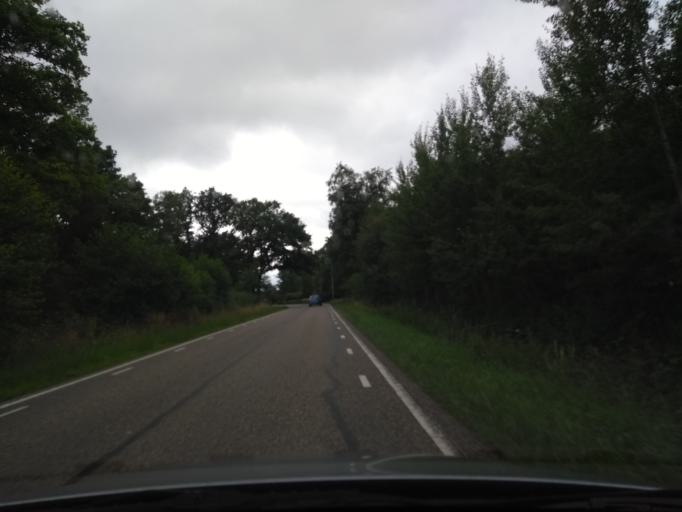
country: NL
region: Drenthe
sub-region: Gemeente Hoogeveen
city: Hoogeveen
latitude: 52.6099
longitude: 6.3804
